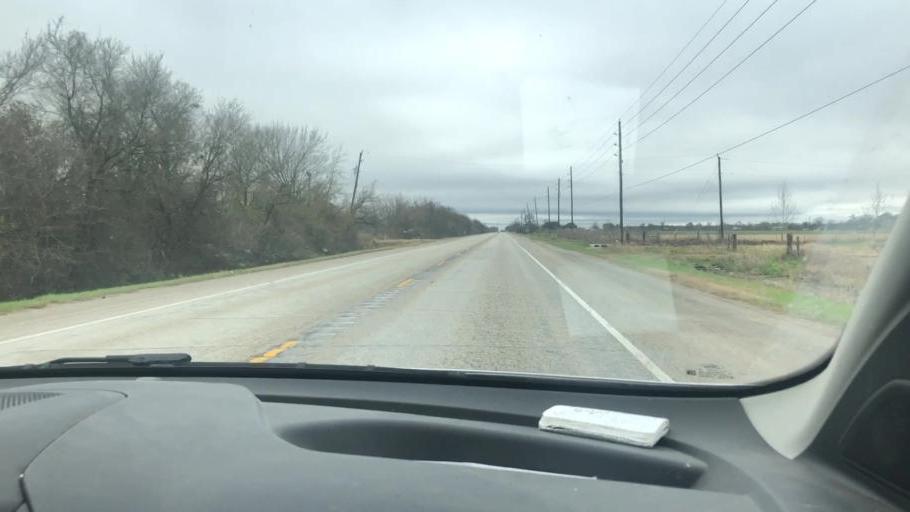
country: US
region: Texas
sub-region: Wharton County
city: Wharton
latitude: 29.2773
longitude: -96.0641
